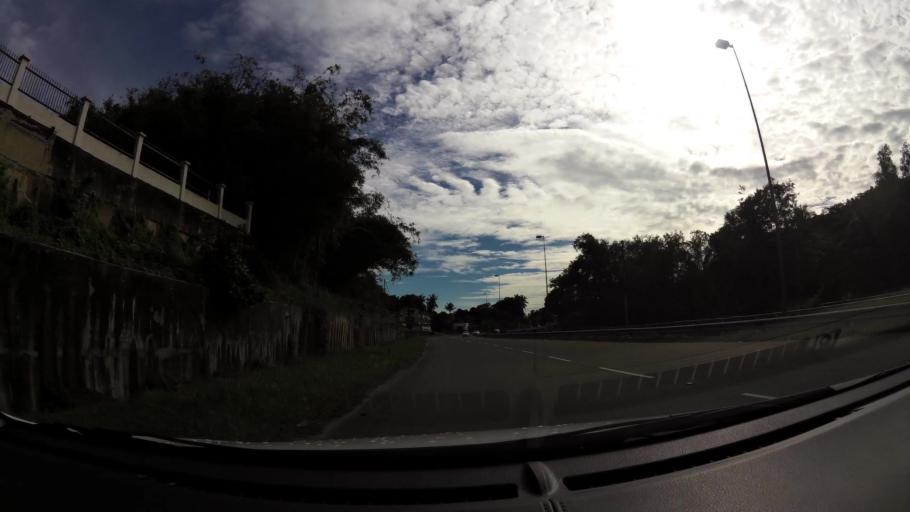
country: BN
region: Brunei and Muara
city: Bandar Seri Begawan
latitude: 4.8903
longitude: 114.9627
